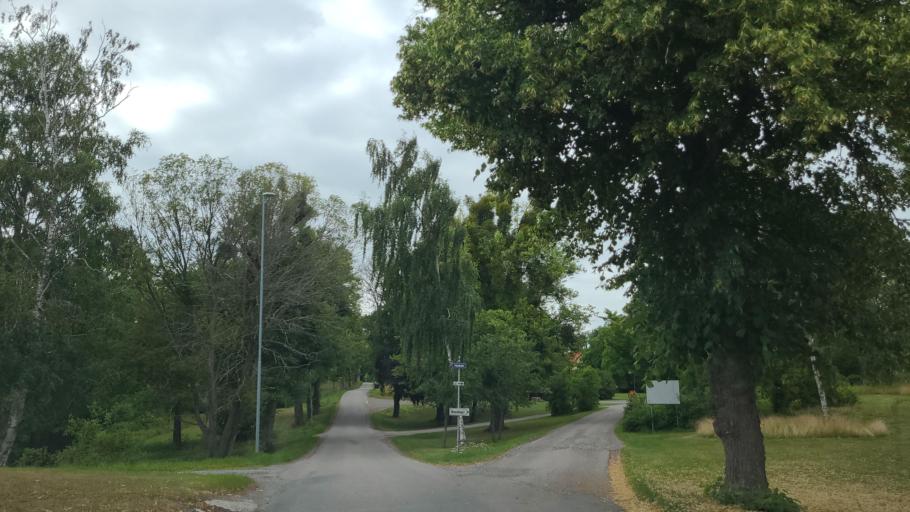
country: SE
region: Stockholm
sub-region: Upplands-Bro Kommun
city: Bro
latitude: 59.5071
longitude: 17.5710
